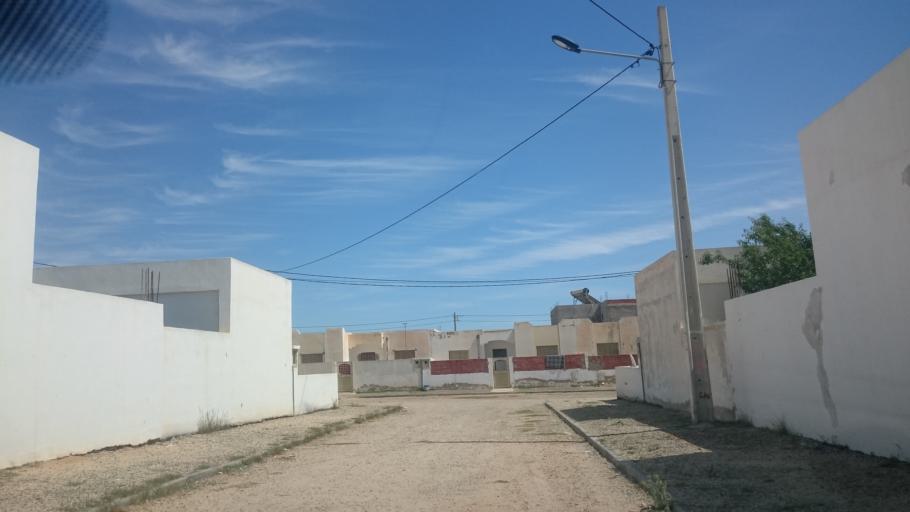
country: TN
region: Safaqis
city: Sfax
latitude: 34.7478
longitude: 10.5131
